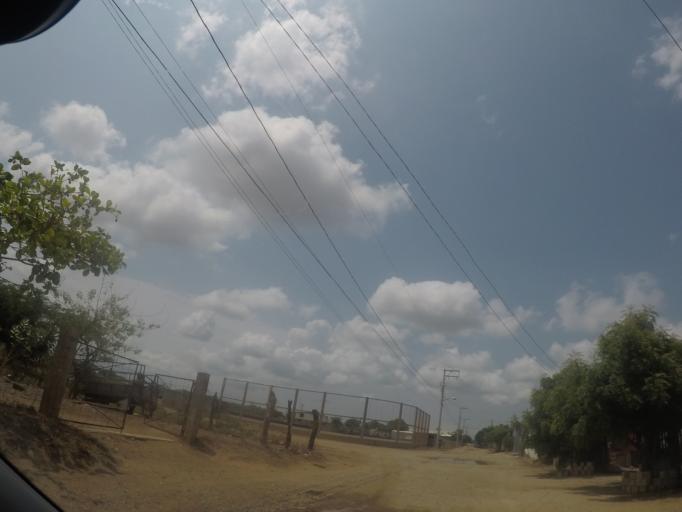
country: MX
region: Oaxaca
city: El Espinal
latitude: 16.5582
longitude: -94.9467
